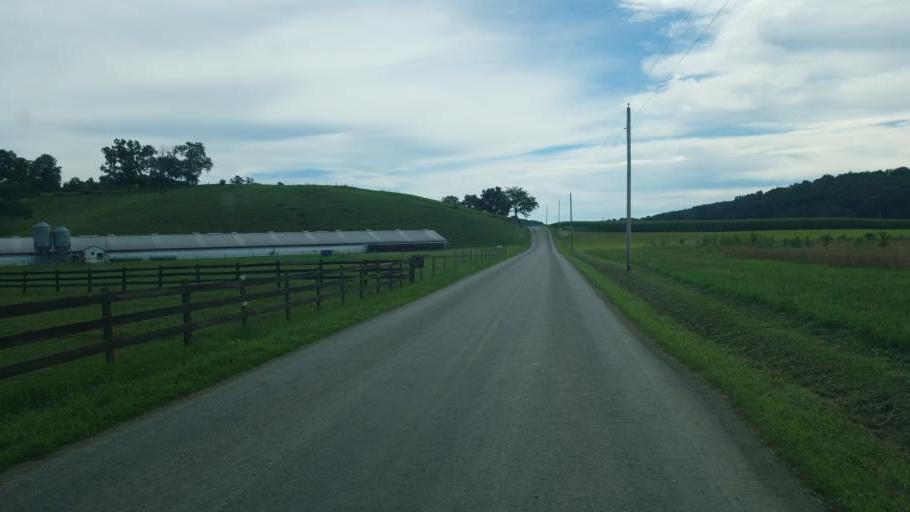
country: US
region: Ohio
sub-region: Holmes County
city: Millersburg
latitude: 40.4743
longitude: -81.8480
